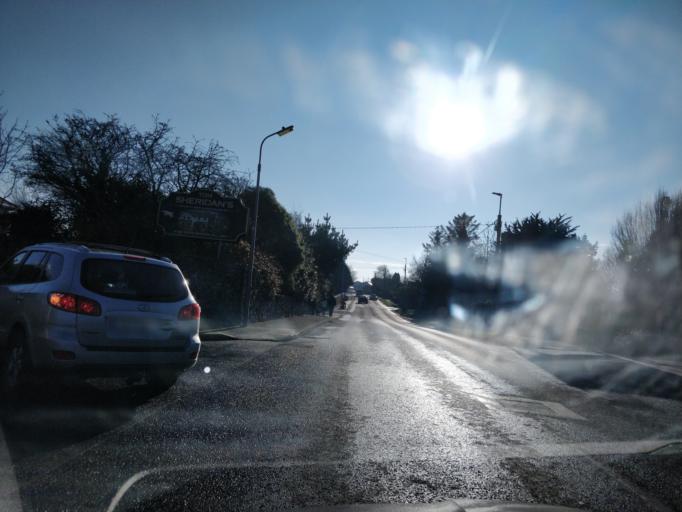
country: IE
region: Connaught
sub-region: County Galway
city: Bearna
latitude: 53.2675
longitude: -9.1066
